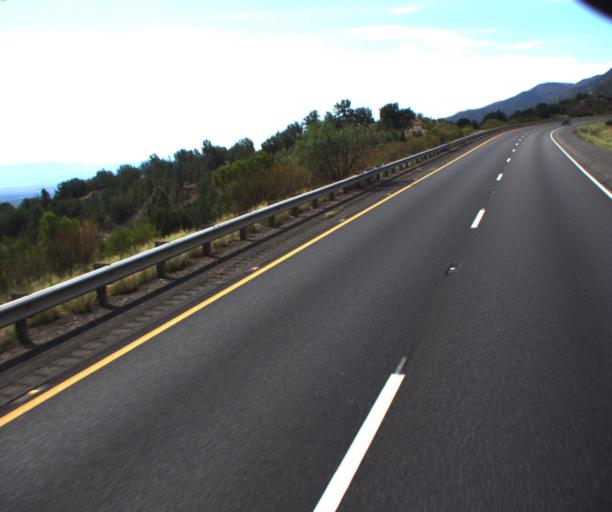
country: US
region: Arizona
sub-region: Yavapai County
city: Camp Verde
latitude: 34.5465
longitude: -111.9092
